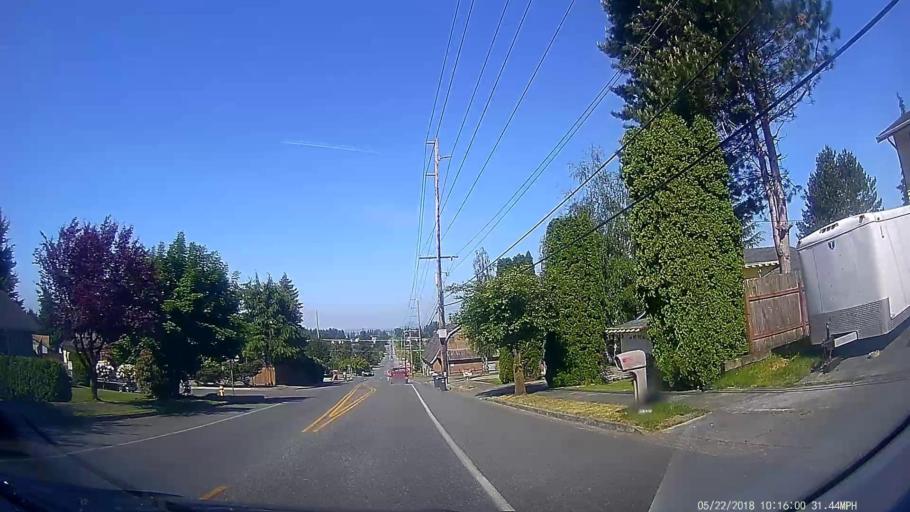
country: US
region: Washington
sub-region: Skagit County
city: Mount Vernon
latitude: 48.4429
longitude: -122.3112
